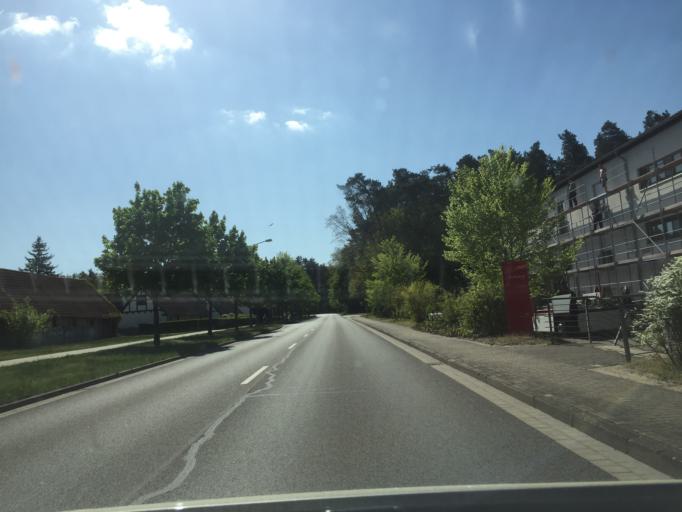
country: DE
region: Mecklenburg-Vorpommern
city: Torgelow
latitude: 53.6258
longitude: 14.0174
